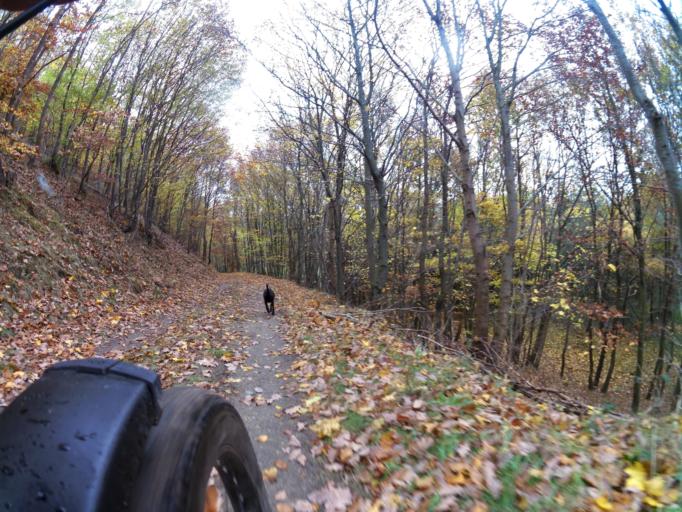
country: PL
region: Pomeranian Voivodeship
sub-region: Powiat wejherowski
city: Gniewino
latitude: 54.7497
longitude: 18.0877
